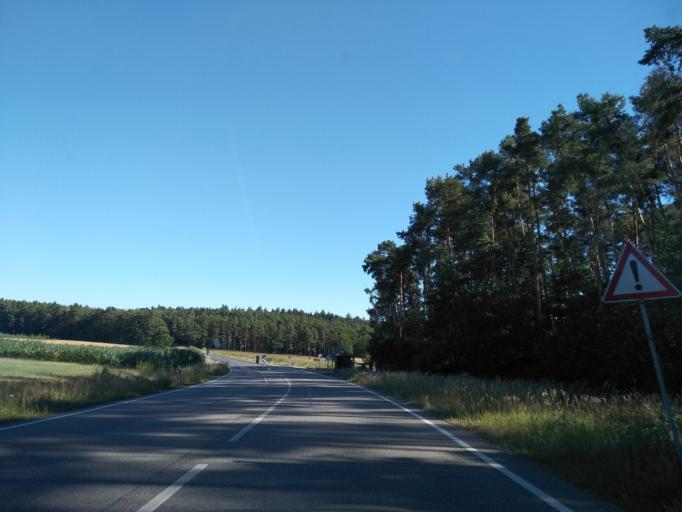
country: DE
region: Bavaria
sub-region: Regierungsbezirk Mittelfranken
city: Rottenbach
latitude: 49.6476
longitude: 10.9200
